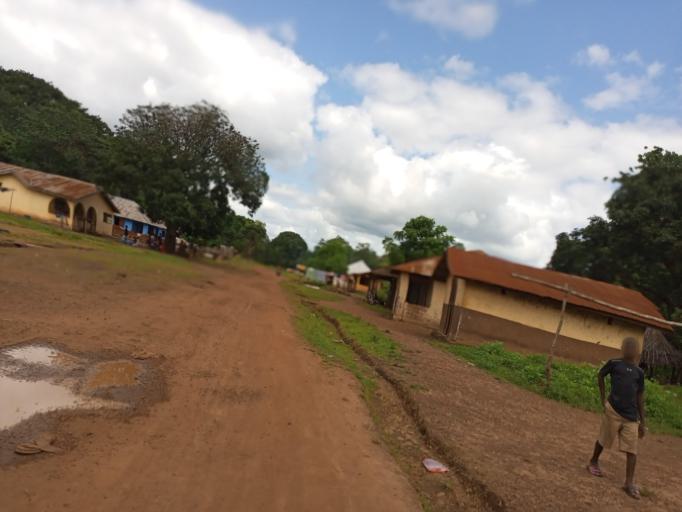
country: SL
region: Northern Province
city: Kamakwie
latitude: 9.5076
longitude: -12.2250
